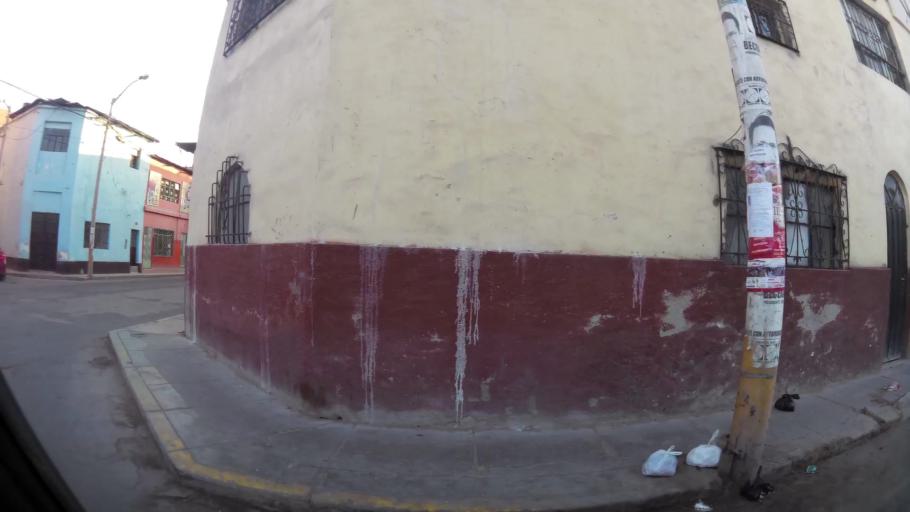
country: PE
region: Lambayeque
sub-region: Provincia de Chiclayo
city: Santa Rosa
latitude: -6.7711
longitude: -79.8335
